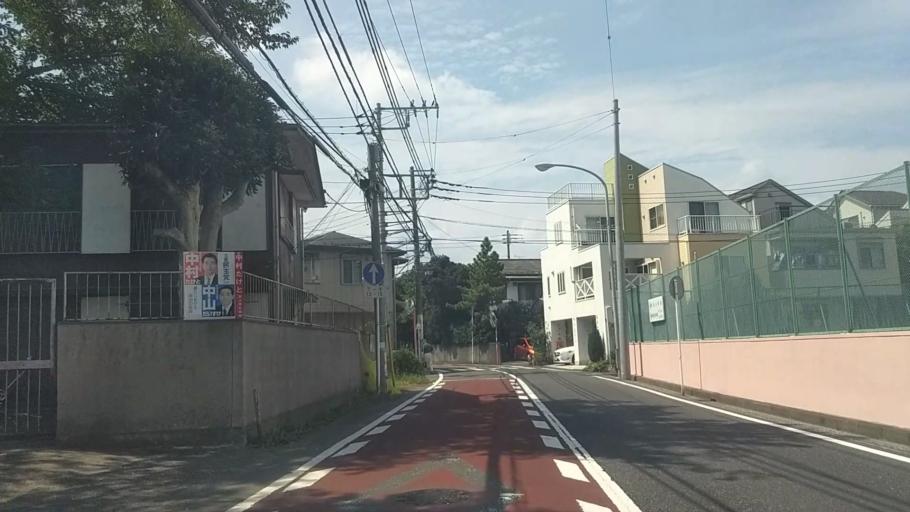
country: JP
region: Kanagawa
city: Yokohama
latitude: 35.4816
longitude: 139.6194
